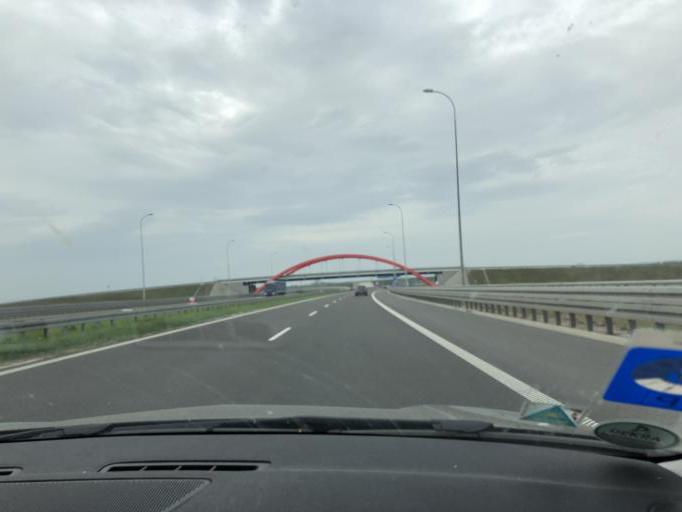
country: PL
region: Subcarpathian Voivodeship
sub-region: Powiat przeworski
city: Gorliczyna
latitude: 50.0842
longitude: 22.4829
